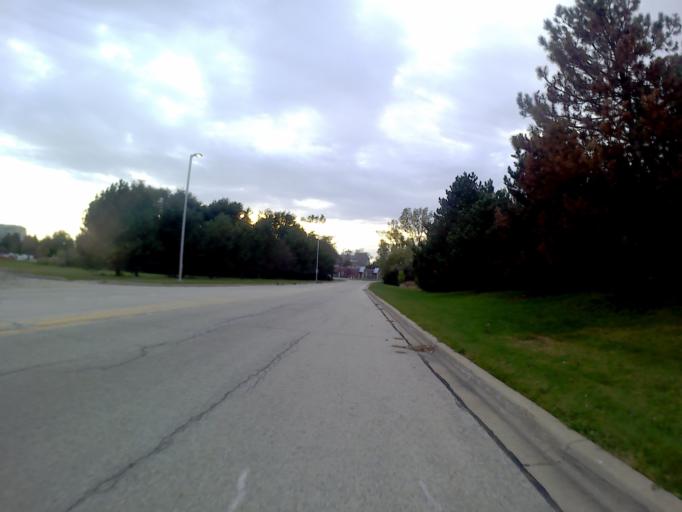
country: US
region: Illinois
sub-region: DuPage County
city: Lisle
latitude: 41.8117
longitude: -88.1119
